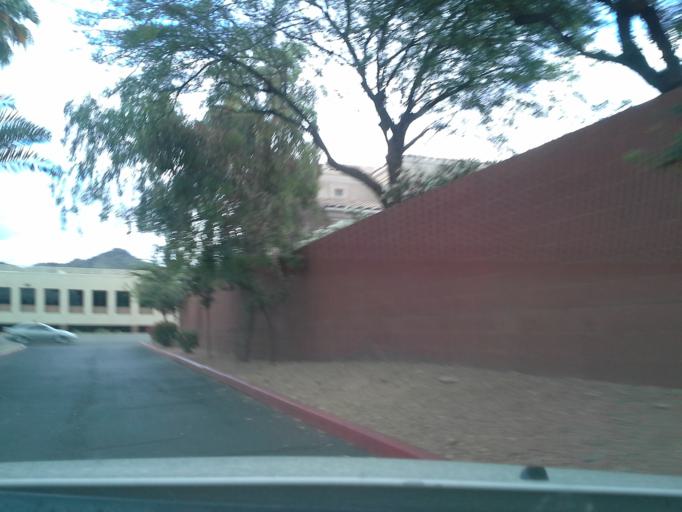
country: US
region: Arizona
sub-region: Maricopa County
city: Paradise Valley
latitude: 33.5546
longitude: -112.0463
